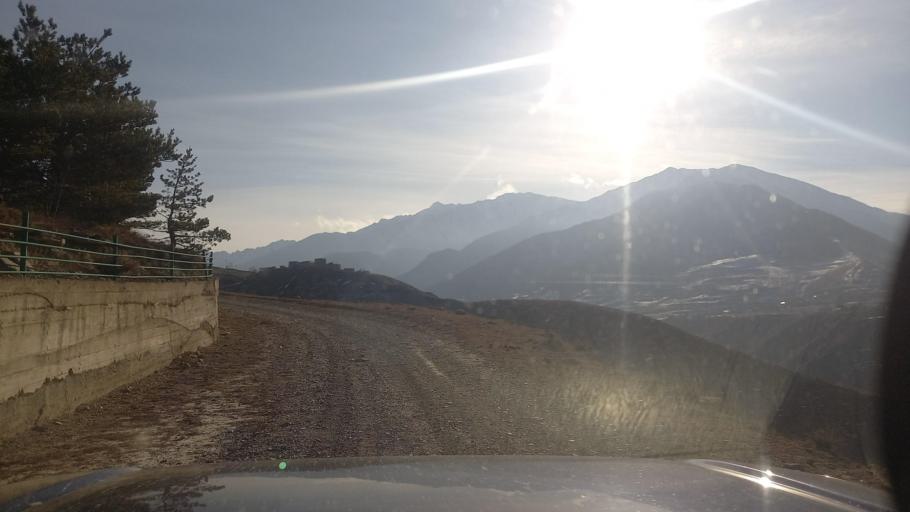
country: RU
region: Ingushetiya
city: Dzhayrakh
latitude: 42.8468
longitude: 44.6552
